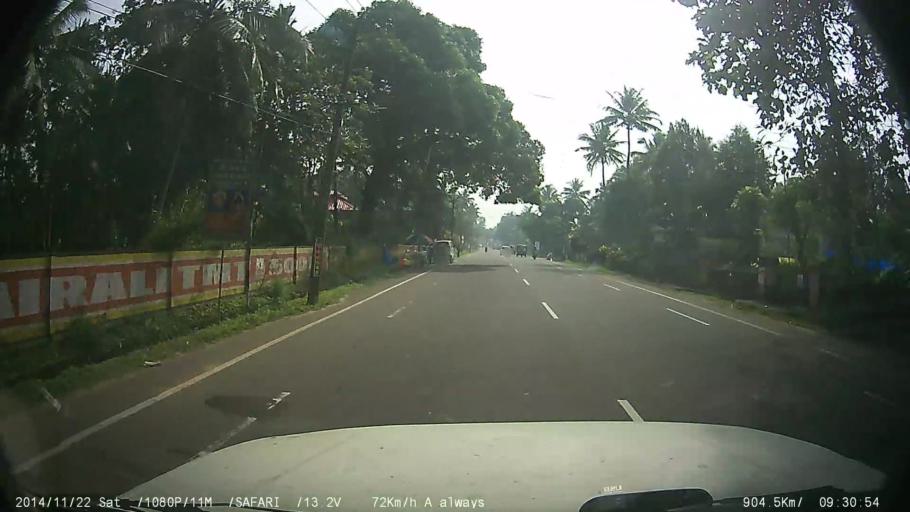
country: IN
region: Kerala
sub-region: Ernakulam
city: Angamali
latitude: 10.1839
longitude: 76.4060
